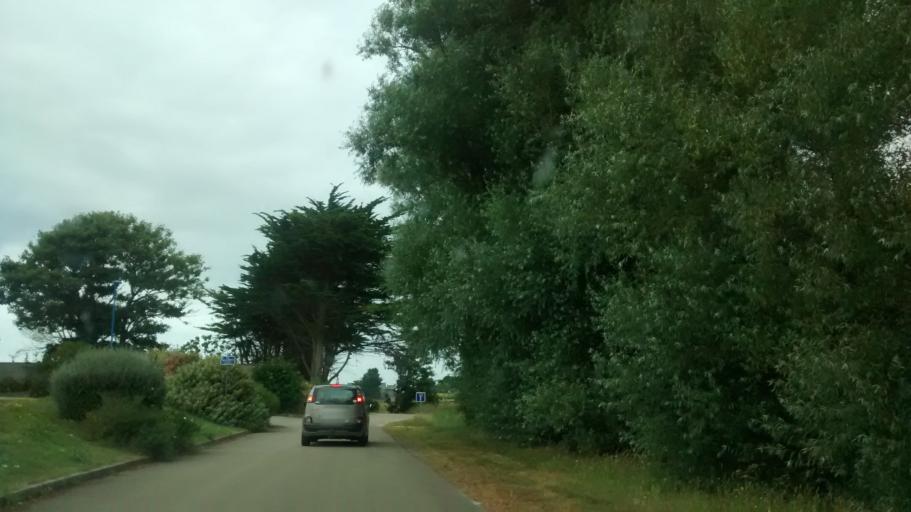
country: FR
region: Brittany
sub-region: Departement du Finistere
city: Guisseny
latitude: 48.6373
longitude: -4.4067
